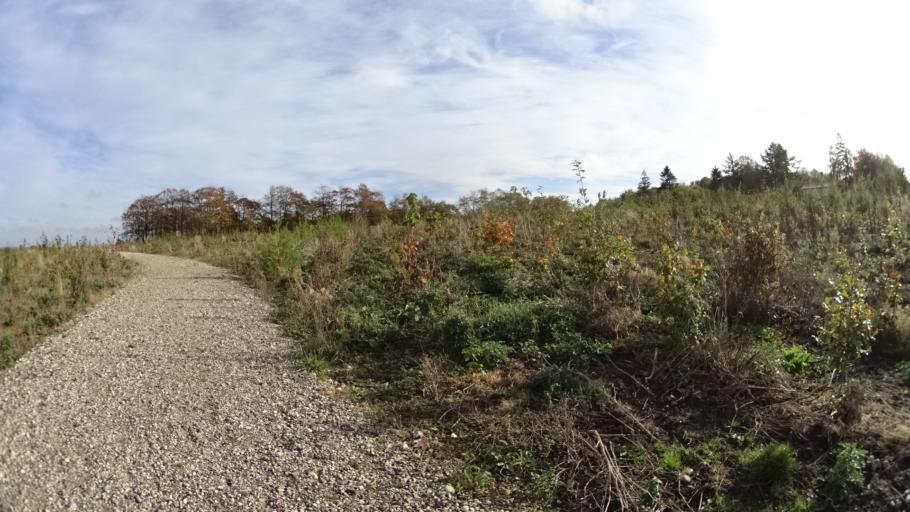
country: DK
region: Central Jutland
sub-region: Arhus Kommune
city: Framlev
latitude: 56.1242
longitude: 10.0217
